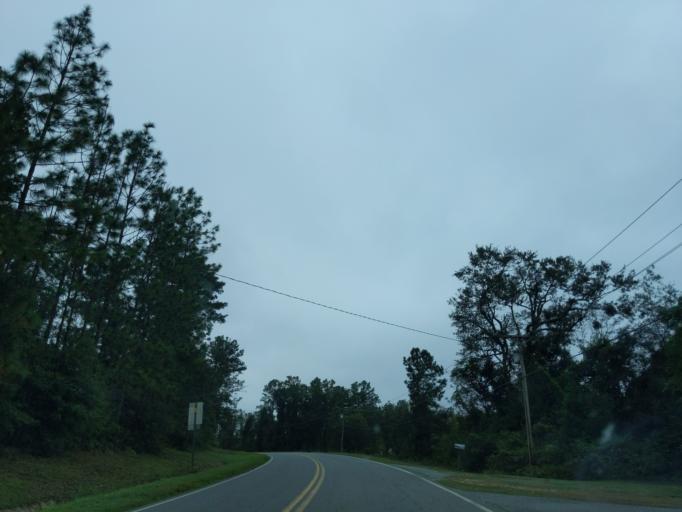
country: US
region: Florida
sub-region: Jackson County
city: Sneads
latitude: 30.7254
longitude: -84.9369
